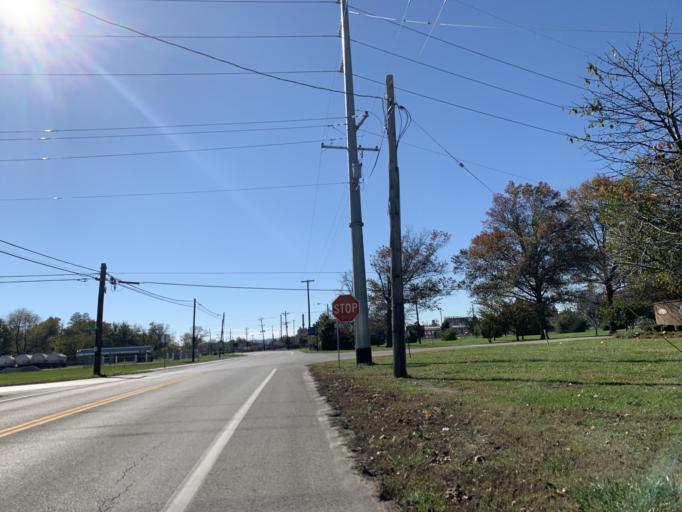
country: US
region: Kentucky
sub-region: Jefferson County
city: Shively
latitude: 38.2127
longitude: -85.8392
